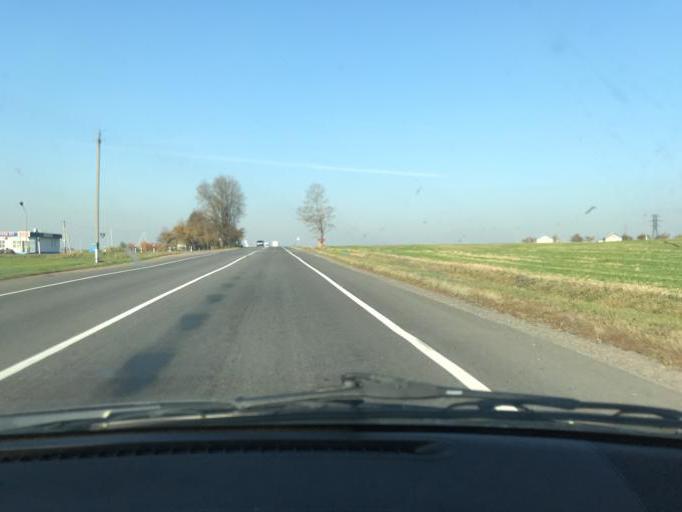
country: BY
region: Mogilev
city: Shklow
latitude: 54.2330
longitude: 30.4518
